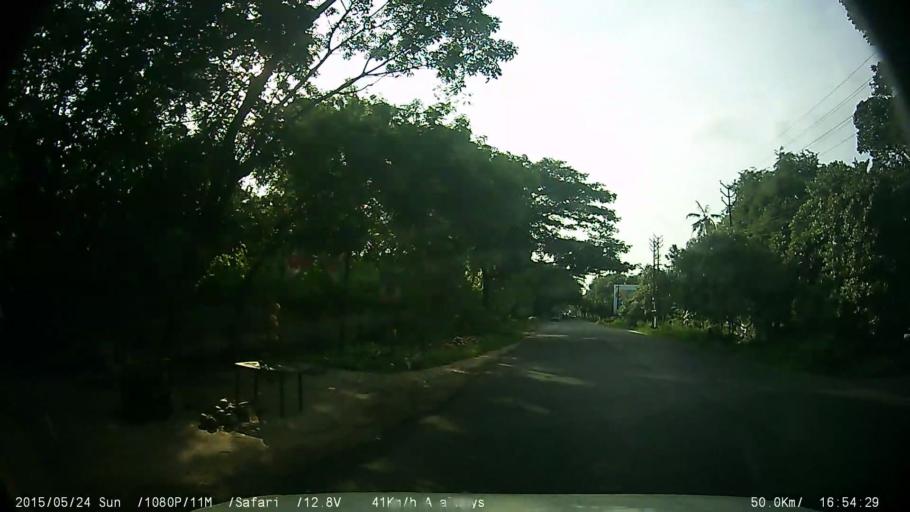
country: IN
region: Kerala
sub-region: Alappuzha
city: Shertallai
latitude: 9.6815
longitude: 76.3351
